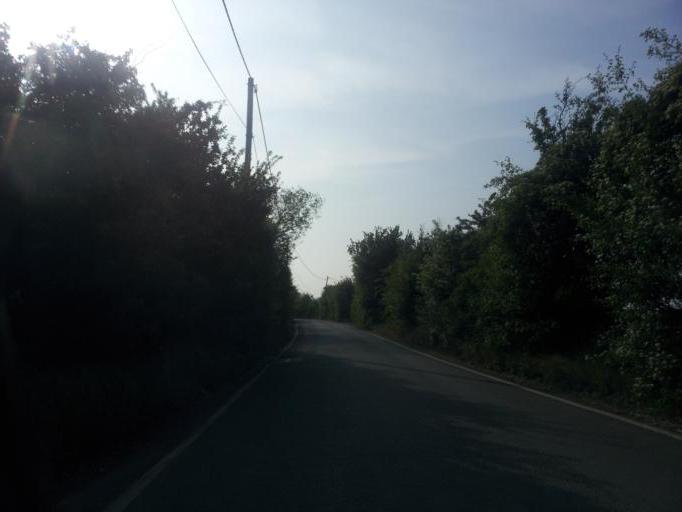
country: GB
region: England
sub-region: Kent
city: Queenborough
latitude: 51.3861
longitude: 0.7294
